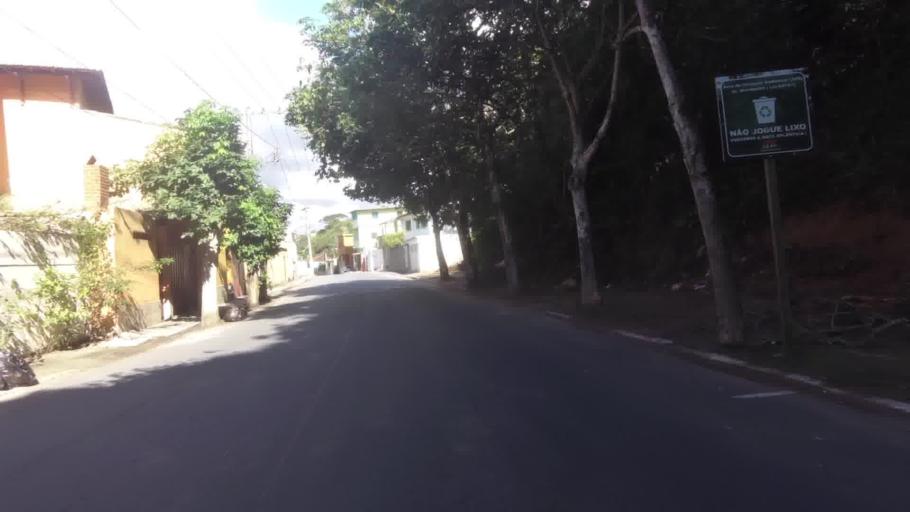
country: BR
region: Espirito Santo
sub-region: Marataizes
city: Marataizes
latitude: -21.0411
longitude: -40.8263
